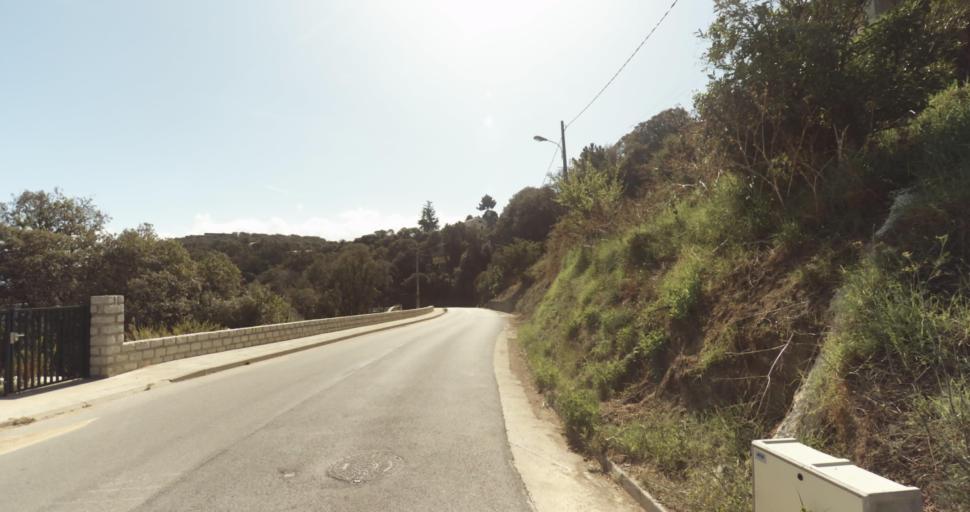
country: FR
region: Corsica
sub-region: Departement de la Corse-du-Sud
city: Ajaccio
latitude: 41.9249
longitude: 8.7189
